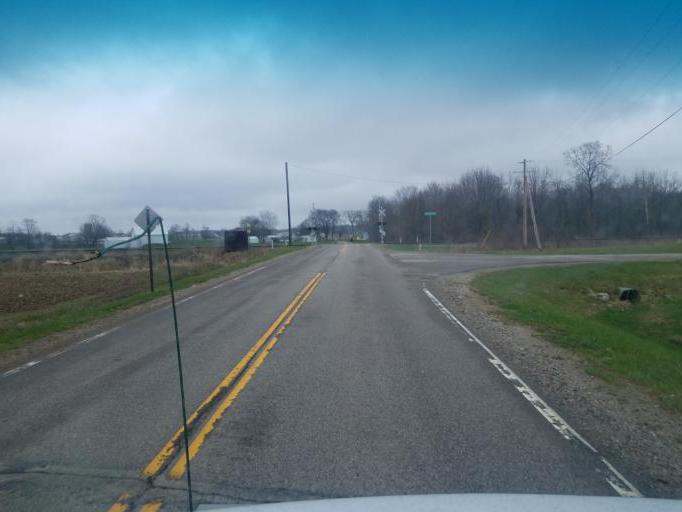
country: US
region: Ohio
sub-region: Richland County
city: Shelby
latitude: 40.9179
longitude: -82.6387
